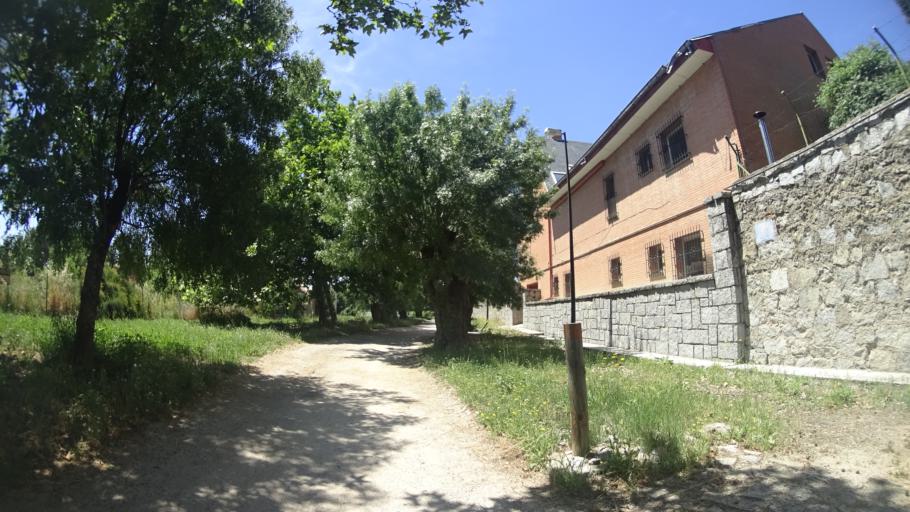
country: ES
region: Madrid
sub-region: Provincia de Madrid
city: Navalquejigo
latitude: 40.6180
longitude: -4.0350
